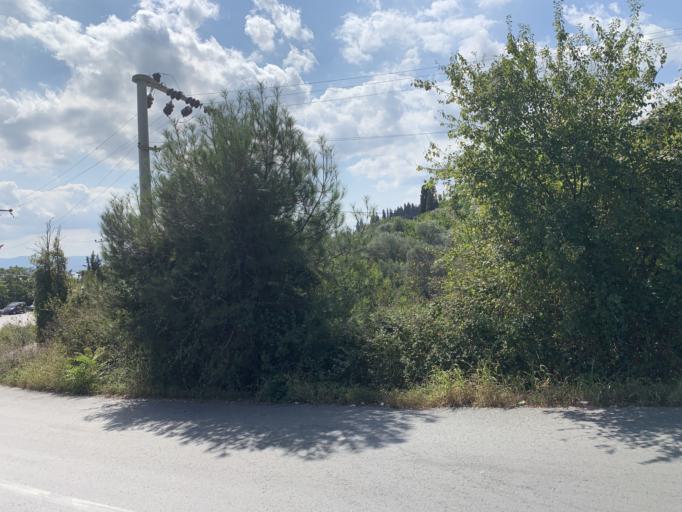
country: TR
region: Kocaeli
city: Darica
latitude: 40.7699
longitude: 29.4259
